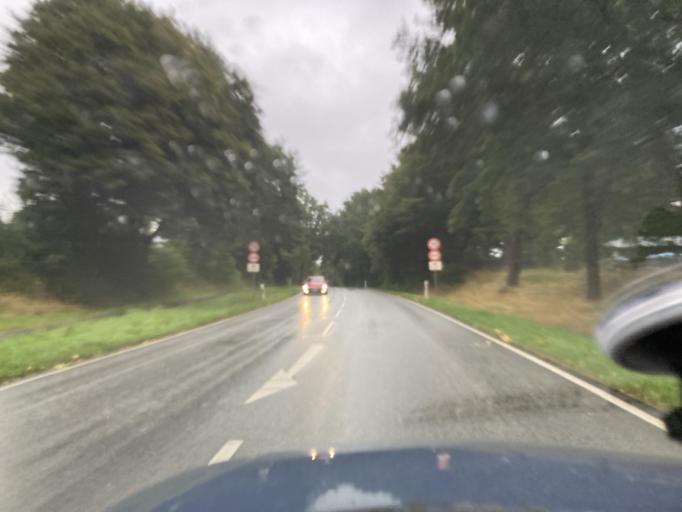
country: DE
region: Schleswig-Holstein
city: Gaushorn
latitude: 54.1984
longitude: 9.2408
